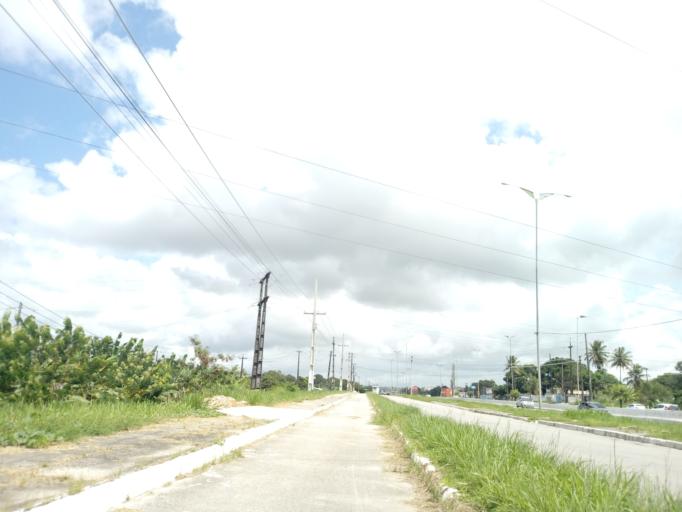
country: BR
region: Pernambuco
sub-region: Cabo De Santo Agostinho
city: Cabo
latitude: -8.2721
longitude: -35.0242
